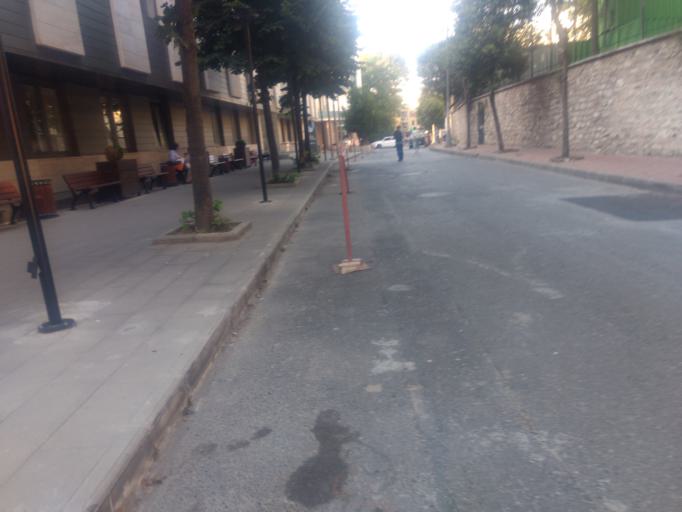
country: TR
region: Istanbul
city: Eminoenue
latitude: 41.0132
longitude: 28.9625
